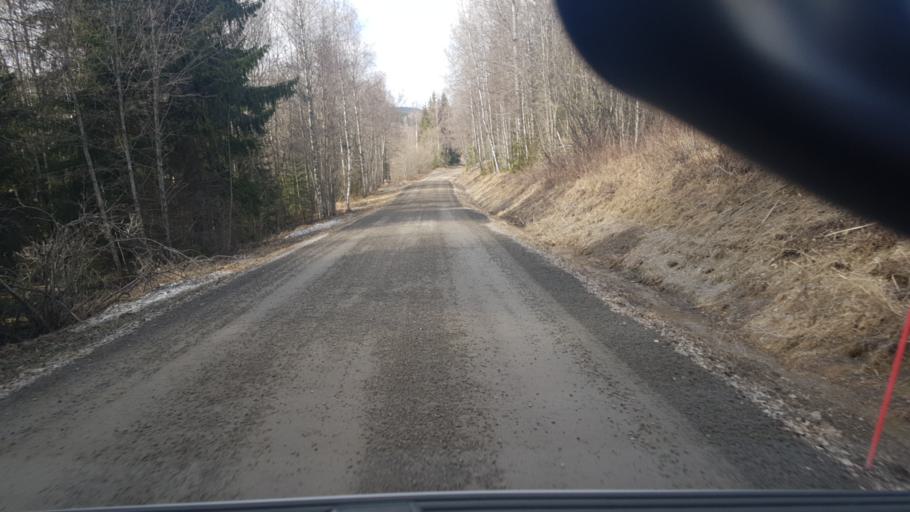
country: SE
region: Vaermland
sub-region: Eda Kommun
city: Amotfors
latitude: 59.7737
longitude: 12.4413
